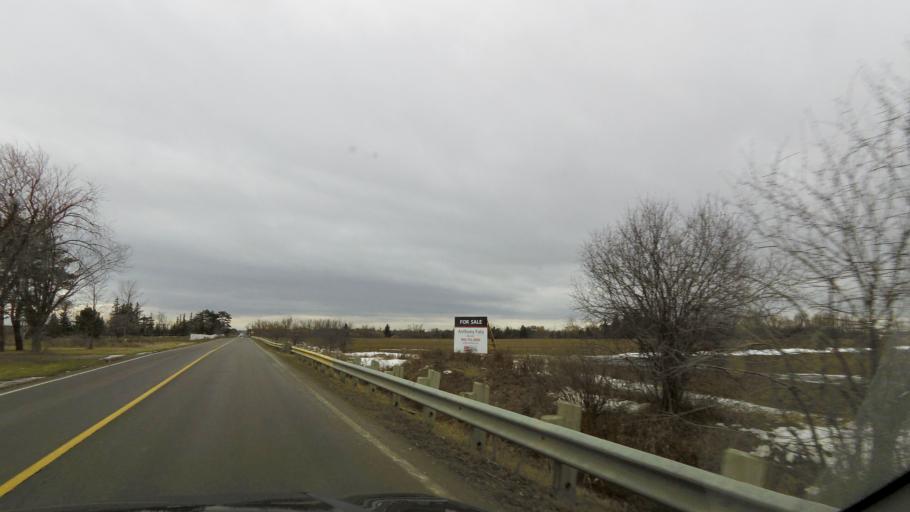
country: CA
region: Ontario
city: Brampton
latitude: 43.8241
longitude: -79.7027
